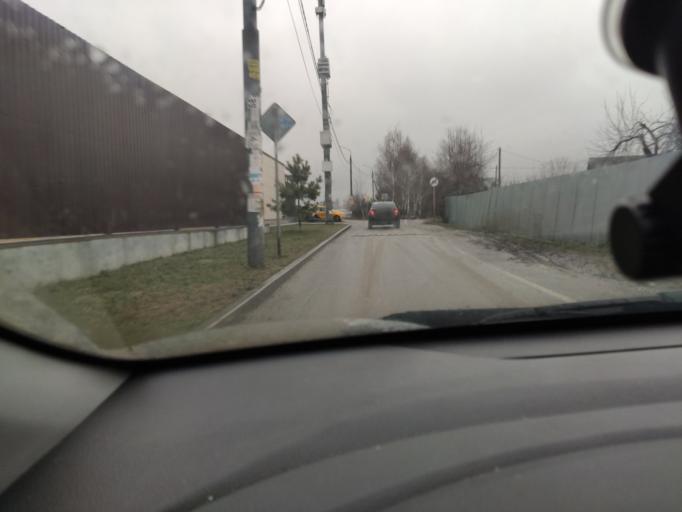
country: RU
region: Moscow
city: Zagor'ye
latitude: 55.5654
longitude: 37.6633
